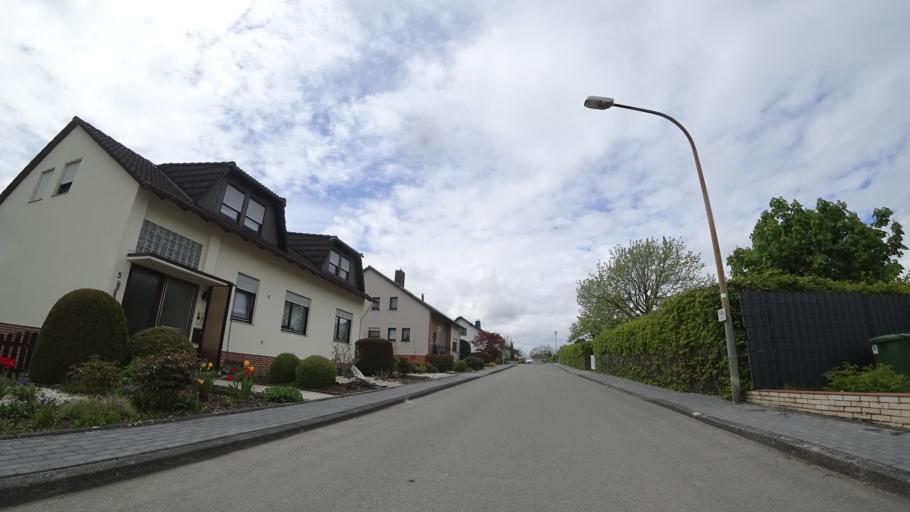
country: DE
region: Hesse
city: Liebenau
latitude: 51.4570
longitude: 9.3117
